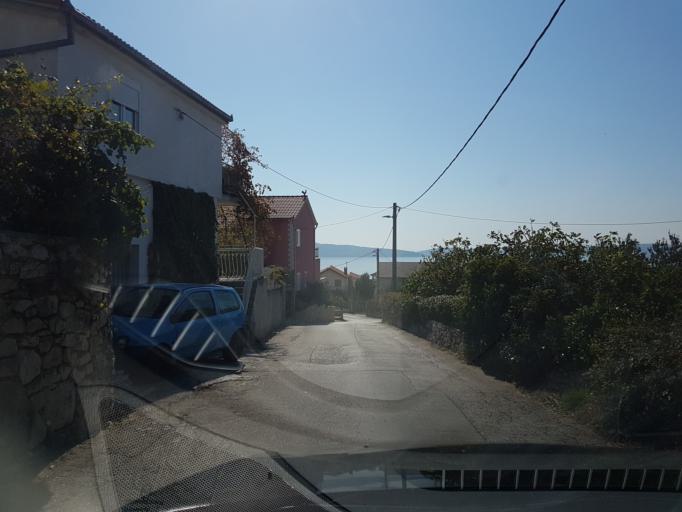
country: HR
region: Splitsko-Dalmatinska
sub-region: Grad Split
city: Split
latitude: 43.5593
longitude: 16.3862
